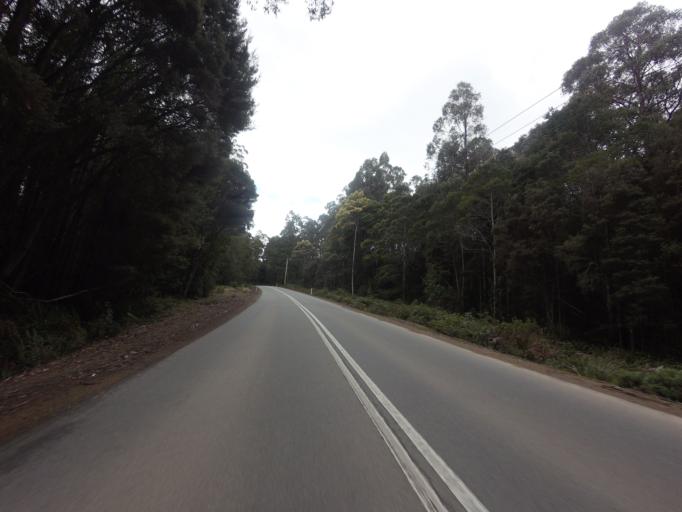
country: AU
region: Tasmania
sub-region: Huon Valley
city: Geeveston
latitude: -43.3829
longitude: 146.9615
